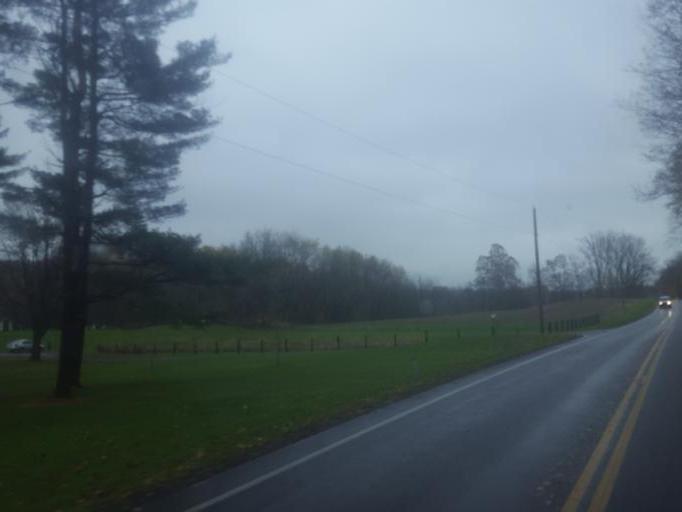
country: US
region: Ohio
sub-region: Richland County
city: Lexington
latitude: 40.7042
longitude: -82.6748
